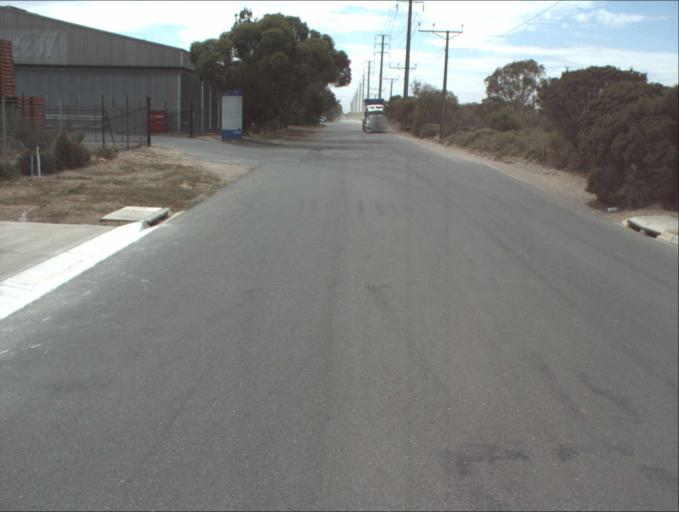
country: AU
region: South Australia
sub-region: Port Adelaide Enfield
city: Birkenhead
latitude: -34.8339
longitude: 138.5200
